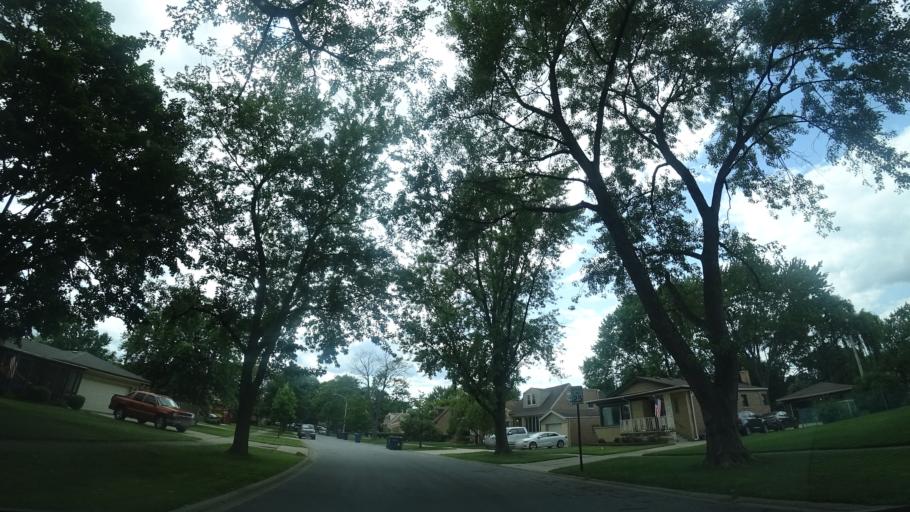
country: US
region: Illinois
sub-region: Cook County
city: Merrionette Park
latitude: 41.6935
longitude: -87.7261
